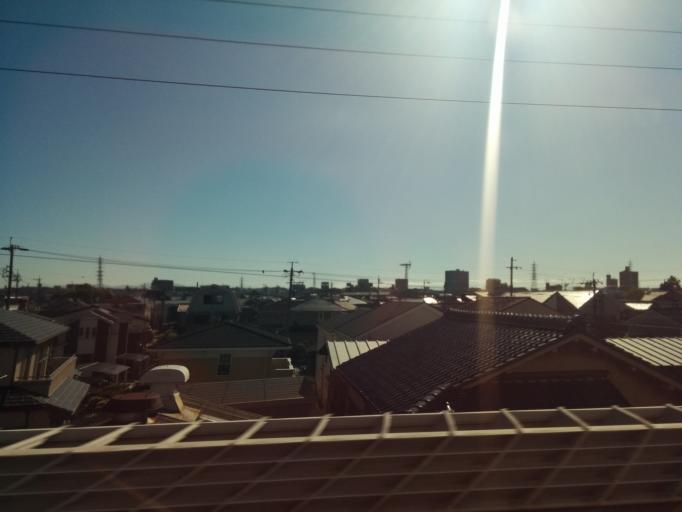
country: JP
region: Aichi
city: Obu
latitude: 35.0779
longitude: 136.9359
